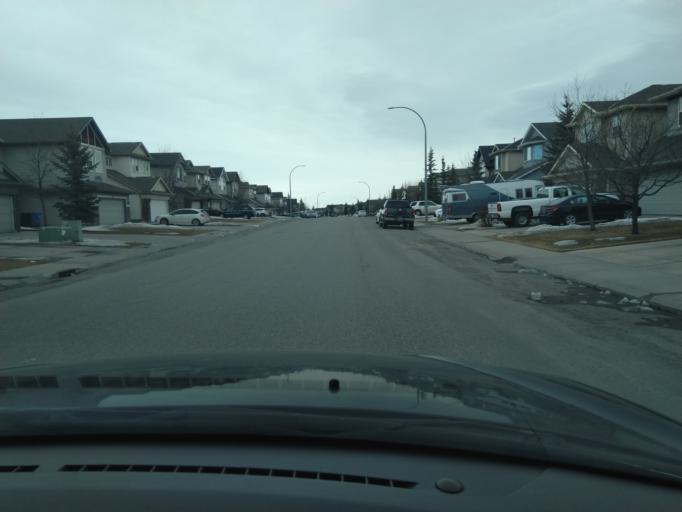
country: CA
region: Alberta
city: Calgary
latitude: 51.1587
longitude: -114.0866
